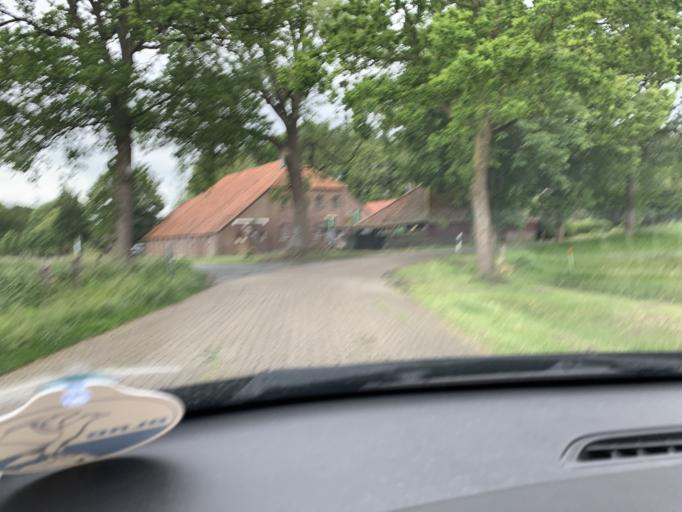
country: DE
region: Lower Saxony
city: Zetel
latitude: 53.3972
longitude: 7.9409
